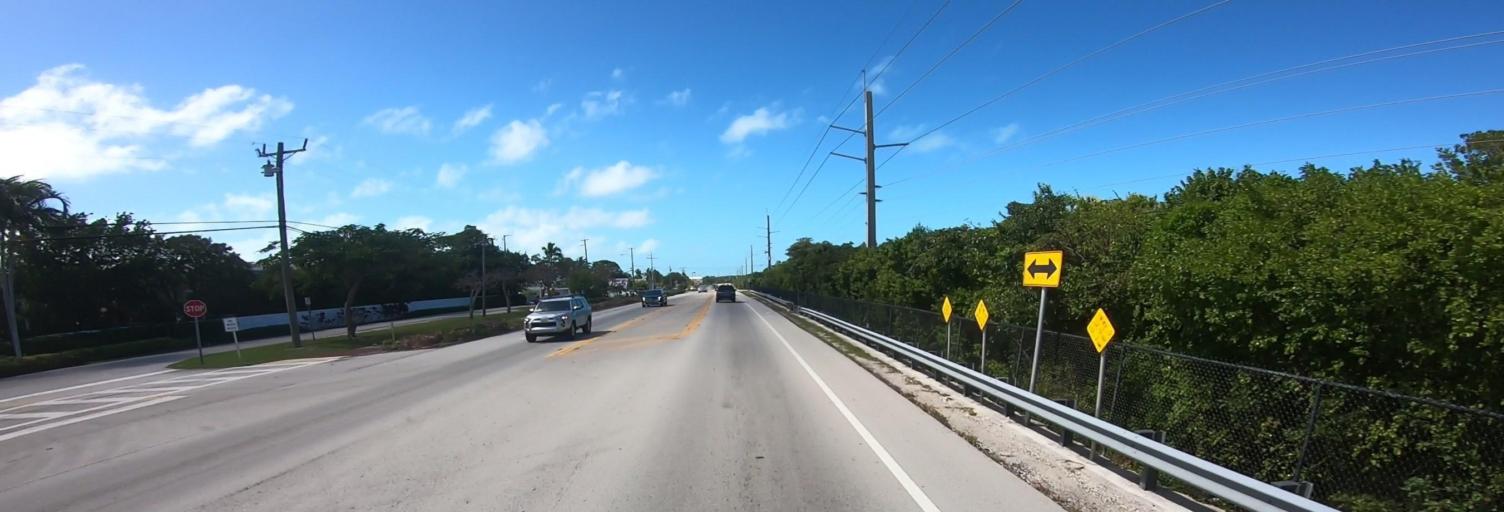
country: US
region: Florida
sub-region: Monroe County
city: Islamorada
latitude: 24.9498
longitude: -80.5946
